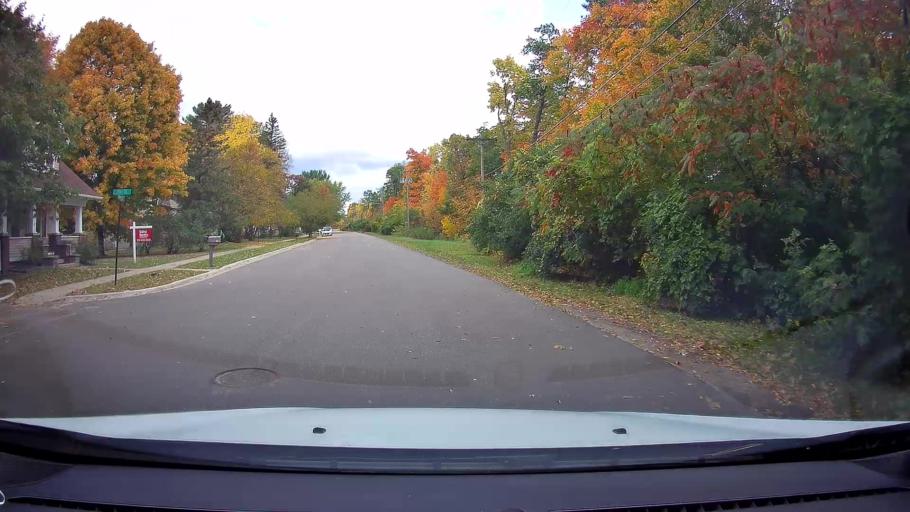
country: US
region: Wisconsin
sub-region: Polk County
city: Saint Croix Falls
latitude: 45.4061
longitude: -92.6506
